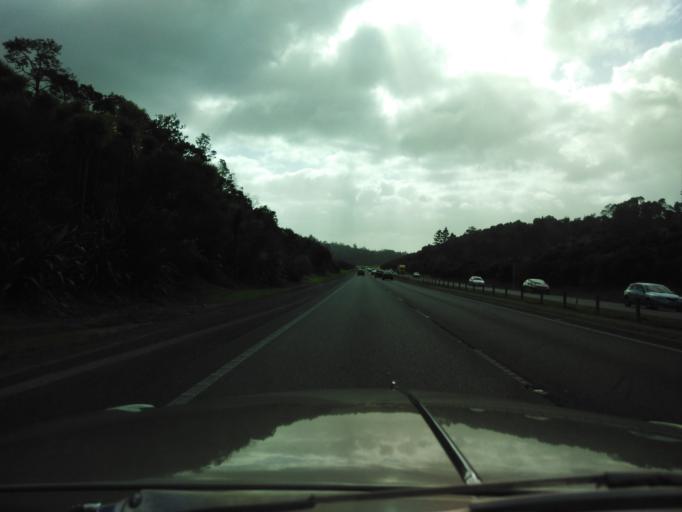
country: NZ
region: Auckland
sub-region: Auckland
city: Rothesay Bay
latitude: -36.6964
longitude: 174.7040
